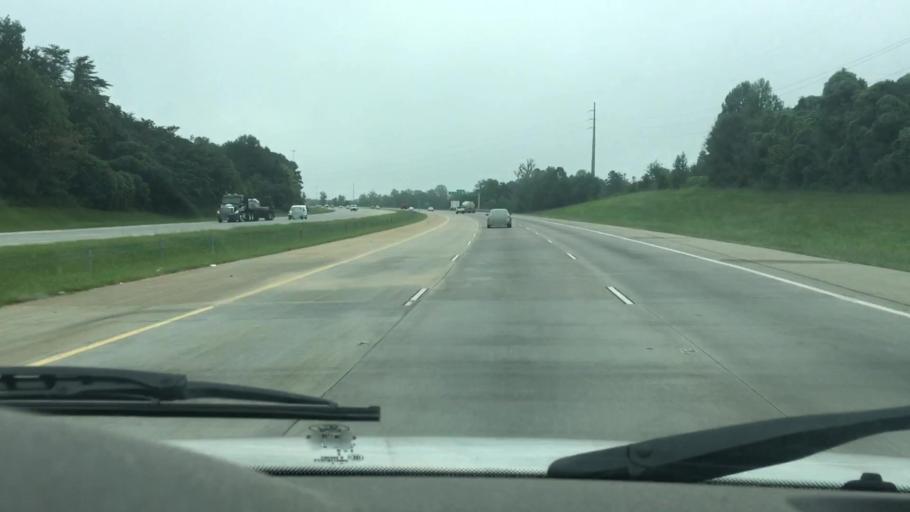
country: US
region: North Carolina
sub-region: Gaston County
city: Mount Holly
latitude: 35.3295
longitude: -80.9199
